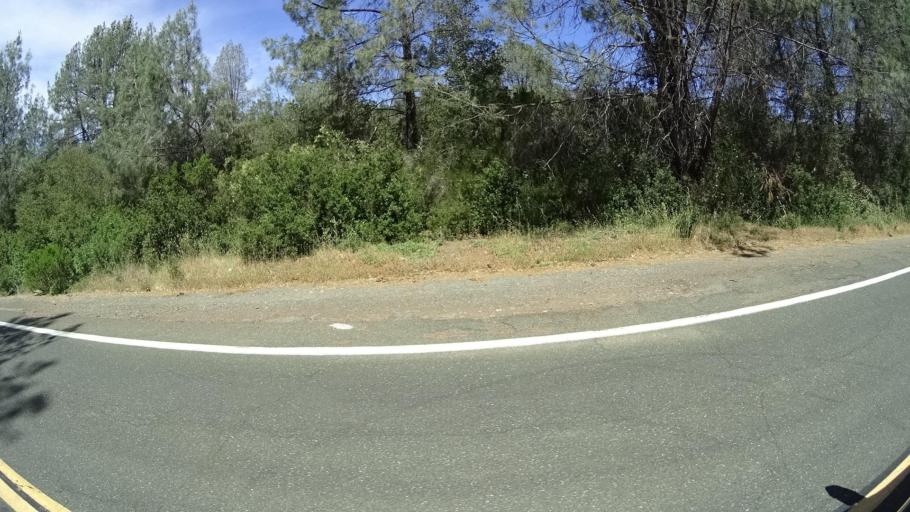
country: US
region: California
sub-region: Lake County
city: Clearlake
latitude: 38.9292
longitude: -122.6573
